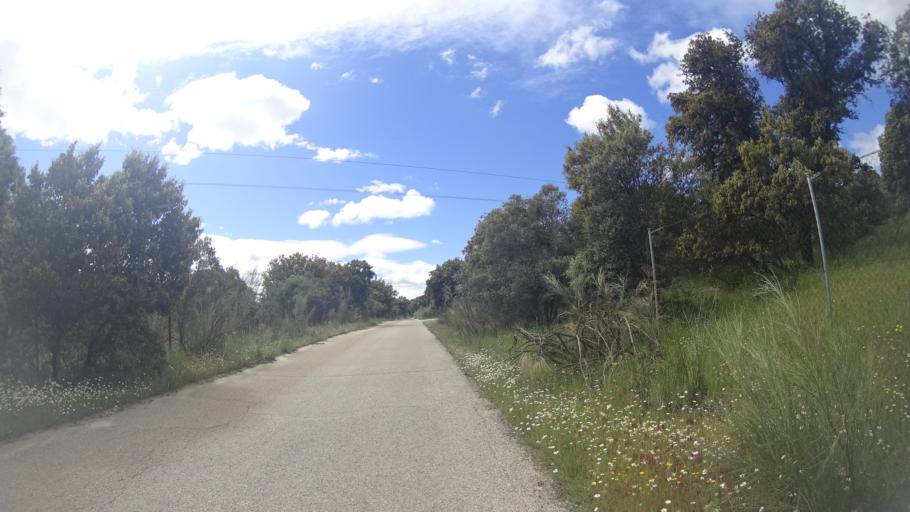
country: ES
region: Madrid
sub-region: Provincia de Madrid
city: Brunete
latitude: 40.4096
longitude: -3.9504
